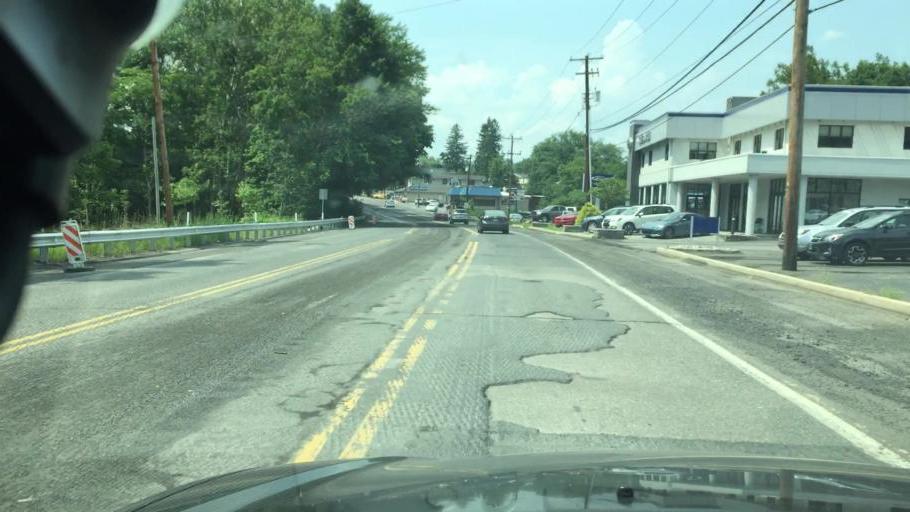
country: US
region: Pennsylvania
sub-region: Monroe County
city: Arlington Heights
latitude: 40.9887
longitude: -75.2099
